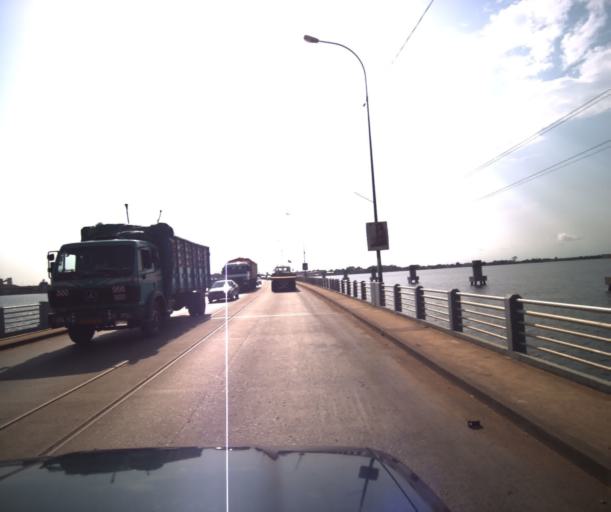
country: CM
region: Littoral
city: Bonaberi
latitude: 4.0726
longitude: 9.6942
